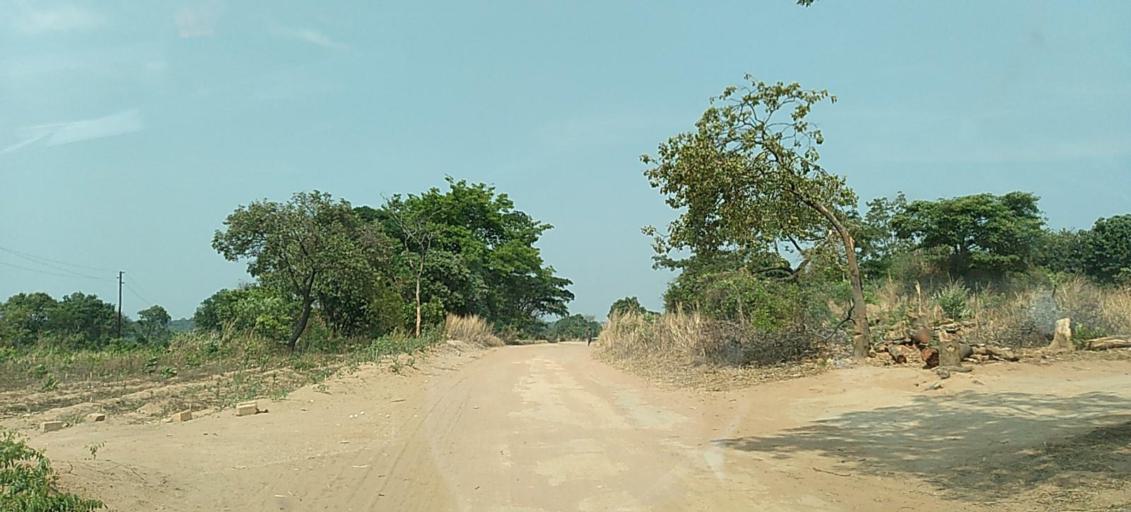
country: ZM
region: Copperbelt
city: Chililabombwe
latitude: -12.3362
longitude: 27.7267
